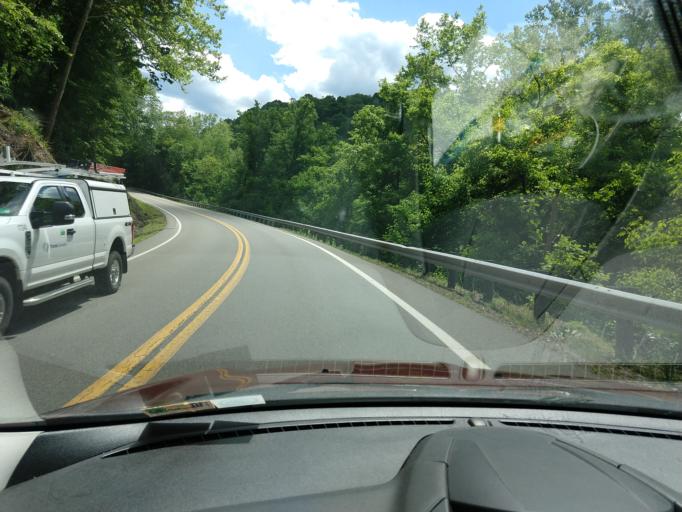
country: US
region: West Virginia
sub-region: Gilmer County
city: Glenville
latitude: 38.8820
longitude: -80.7227
